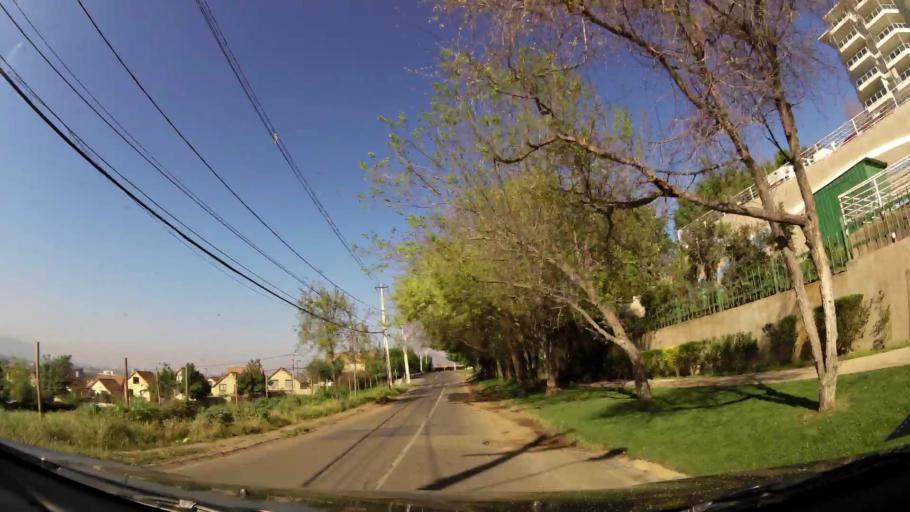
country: CL
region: Santiago Metropolitan
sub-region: Provincia de Chacabuco
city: Chicureo Abajo
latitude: -33.3411
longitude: -70.6731
